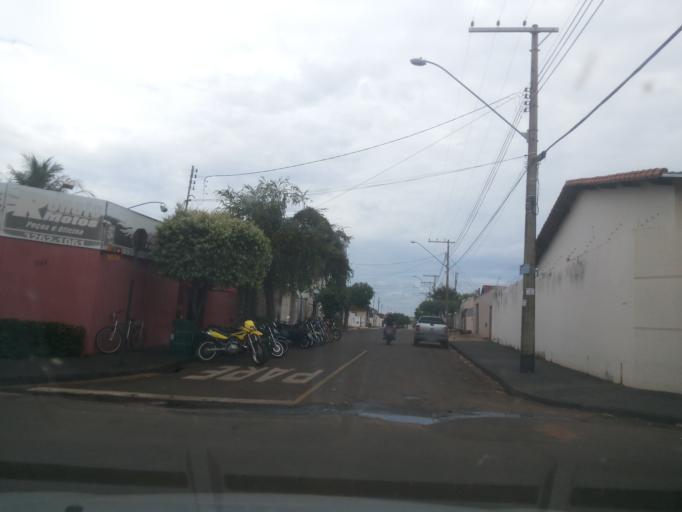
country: BR
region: Minas Gerais
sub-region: Ituiutaba
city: Ituiutaba
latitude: -18.9702
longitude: -49.4731
